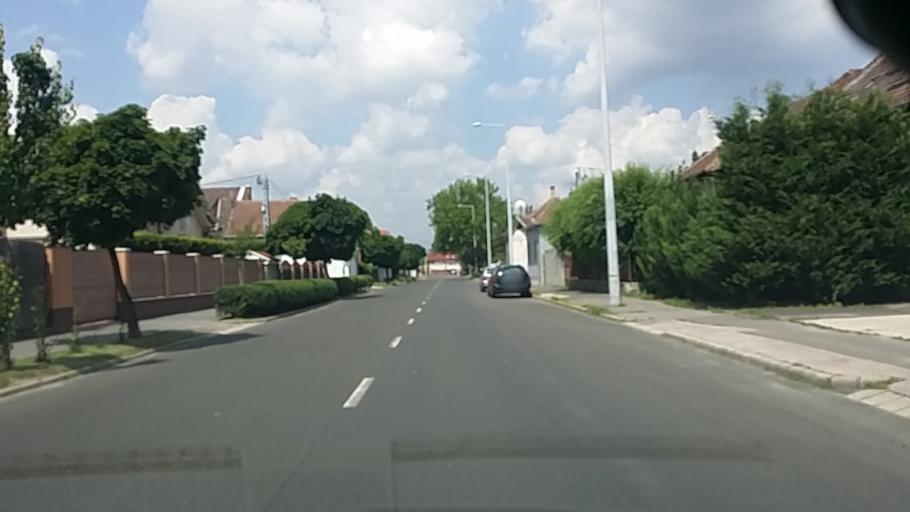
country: HU
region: Budapest
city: Budapest XV. keruelet
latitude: 47.5453
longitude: 19.1293
